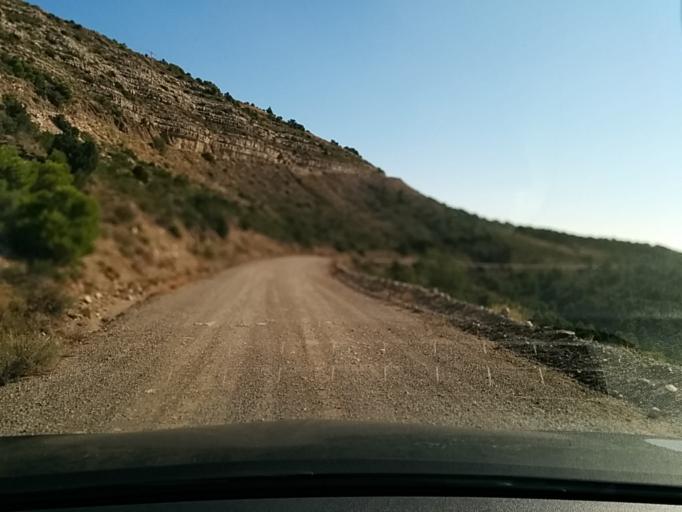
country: ES
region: Aragon
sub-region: Provincia de Zaragoza
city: Novillas
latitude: 42.0181
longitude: -1.3236
